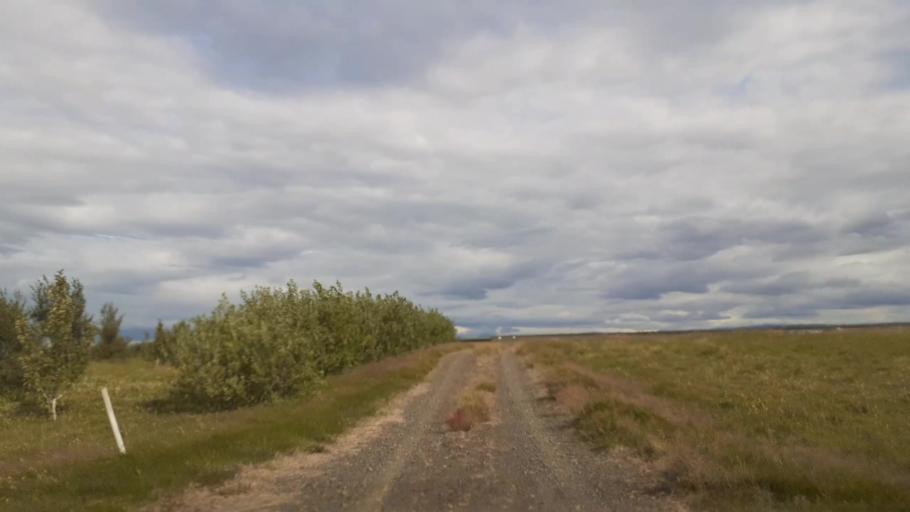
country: IS
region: South
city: Vestmannaeyjar
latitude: 63.7731
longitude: -20.2987
